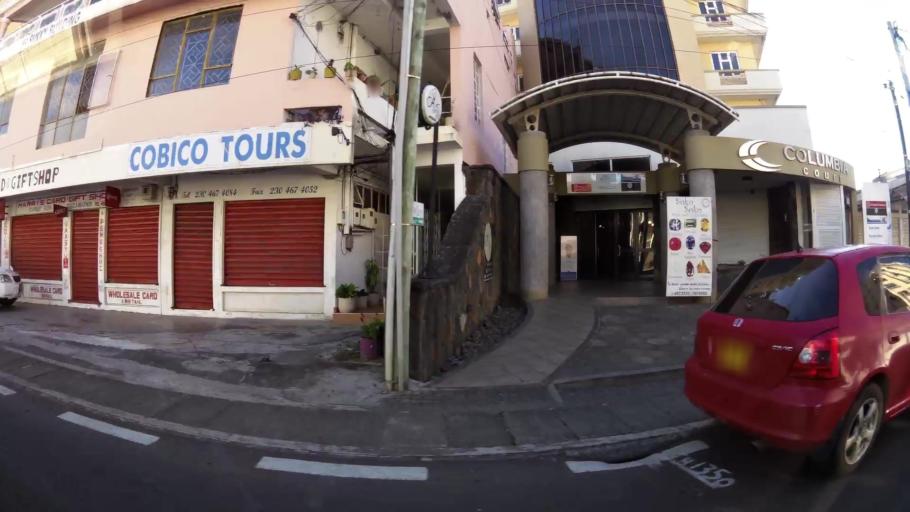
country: MU
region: Plaines Wilhems
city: Quatre Bornes
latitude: -20.2612
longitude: 57.4829
